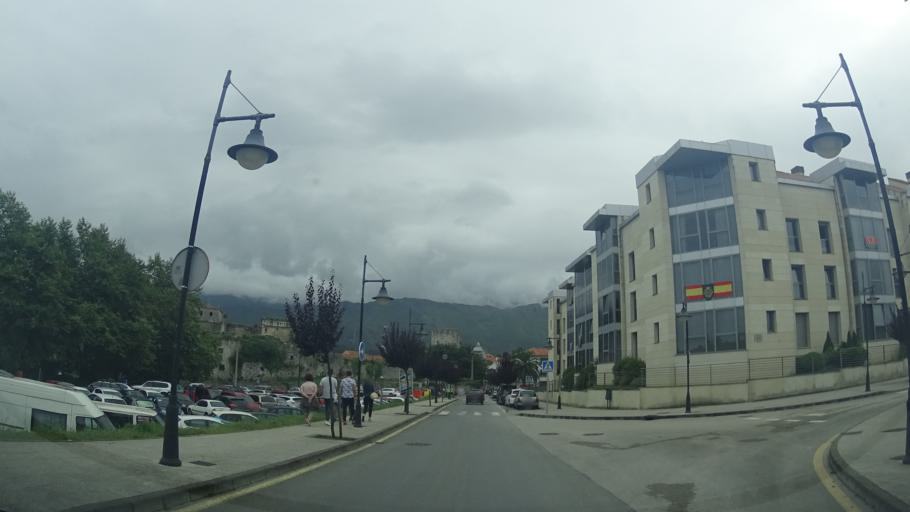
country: ES
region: Asturias
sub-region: Province of Asturias
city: Llanes
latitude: 43.4229
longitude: -4.7548
